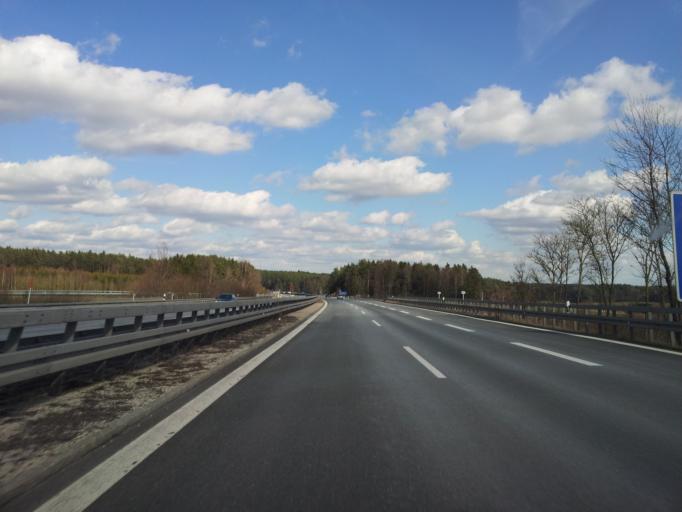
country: DE
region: Bavaria
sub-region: Upper Franconia
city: Stadelhofen
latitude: 50.0005
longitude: 11.2070
